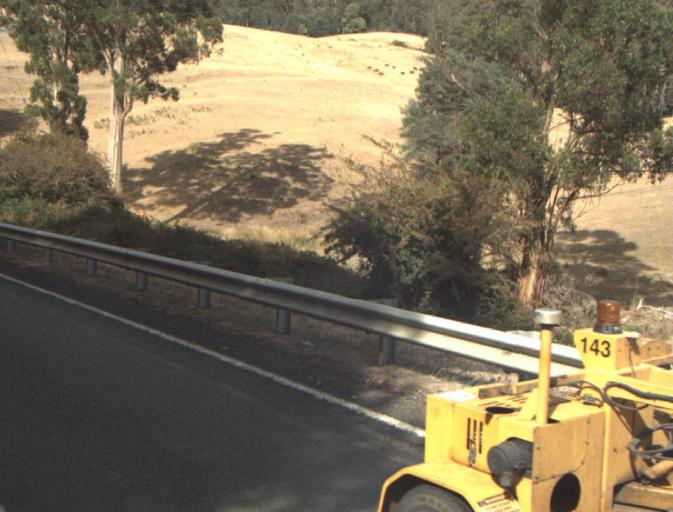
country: AU
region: Tasmania
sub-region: Launceston
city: Mayfield
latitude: -41.2676
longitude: 147.2139
